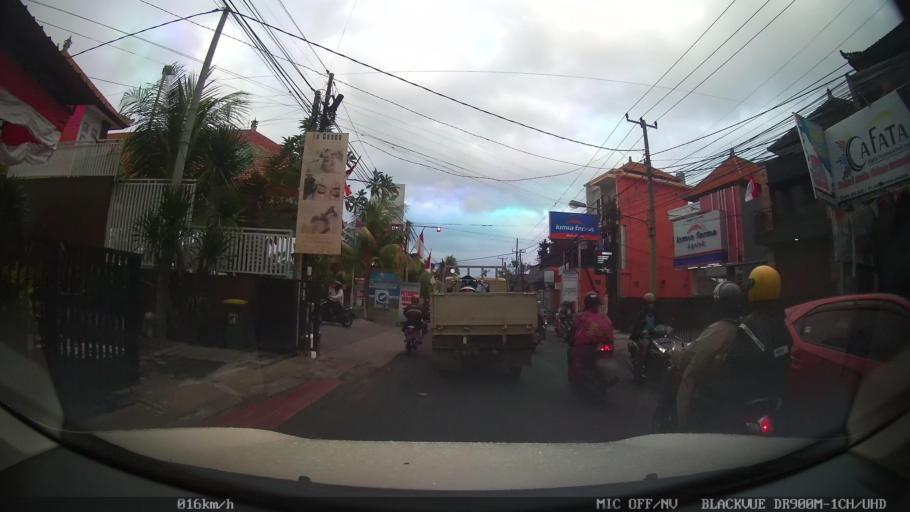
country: ID
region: Bali
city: Banjar Kayangan
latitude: -8.6288
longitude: 115.2243
